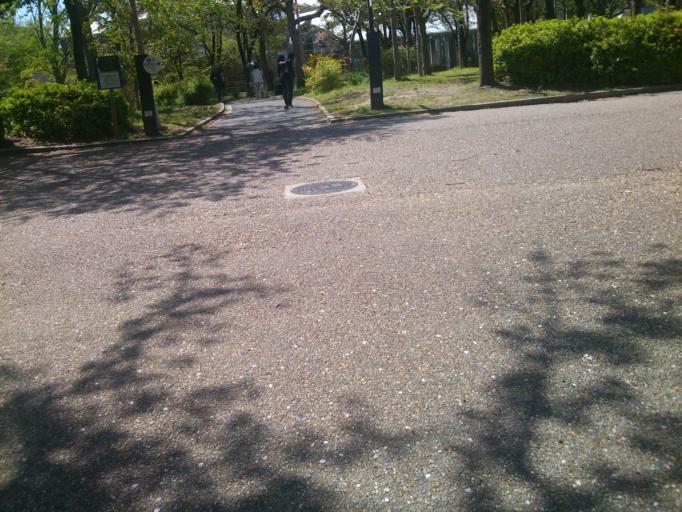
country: JP
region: Osaka
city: Osaka-shi
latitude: 34.6826
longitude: 135.5299
